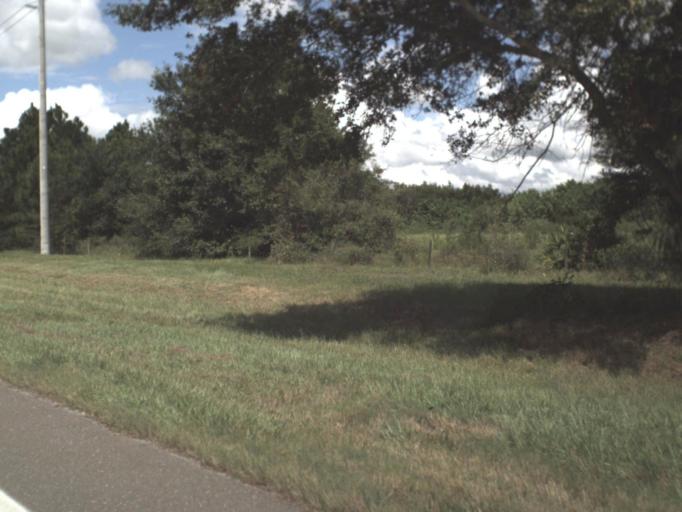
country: US
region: Florida
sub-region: Polk County
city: Mulberry
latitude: 27.7048
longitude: -82.0224
